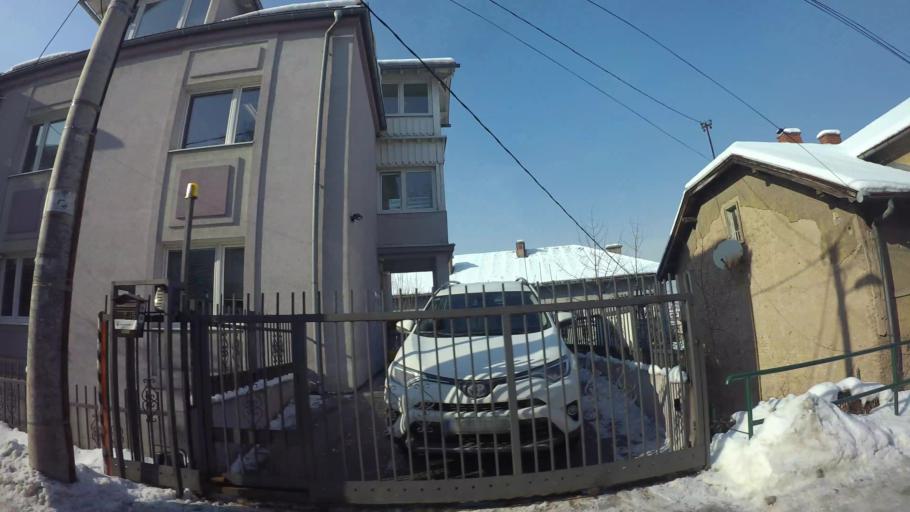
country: BA
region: Federation of Bosnia and Herzegovina
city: Kobilja Glava
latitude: 43.8507
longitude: 18.4042
